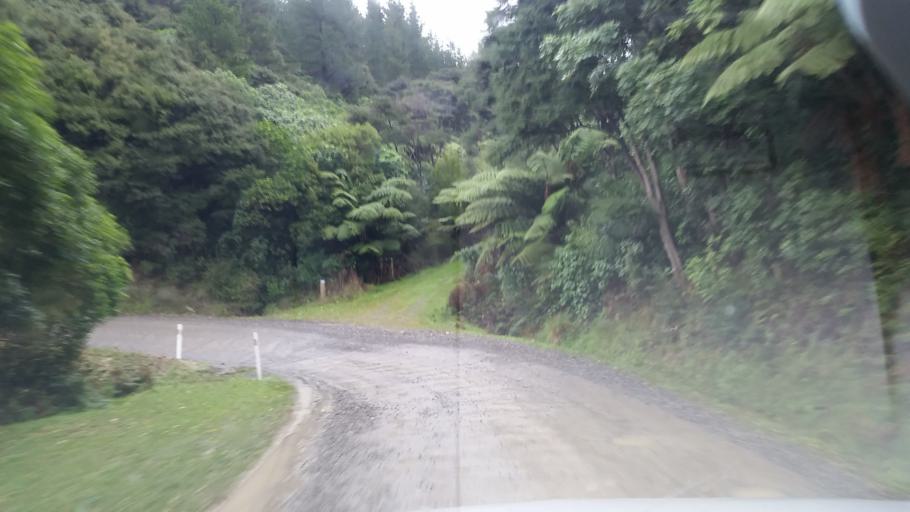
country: NZ
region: Marlborough
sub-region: Marlborough District
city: Picton
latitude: -41.1763
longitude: 174.0564
